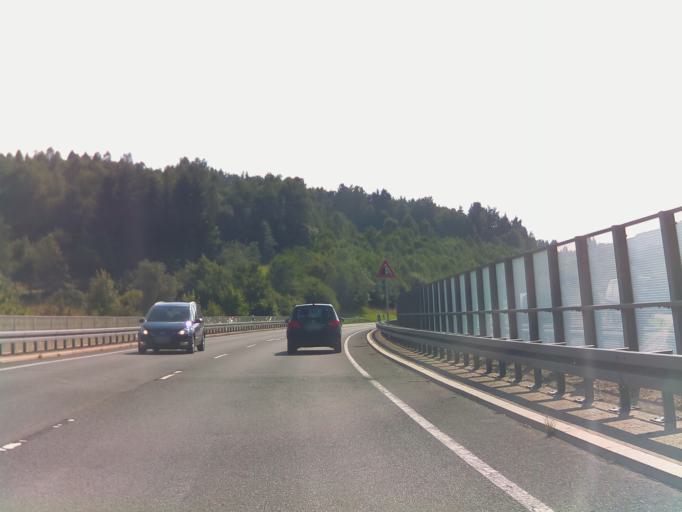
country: DE
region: Bavaria
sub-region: Regierungsbezirk Unterfranken
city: Wildflecken
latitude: 50.3746
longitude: 9.9142
